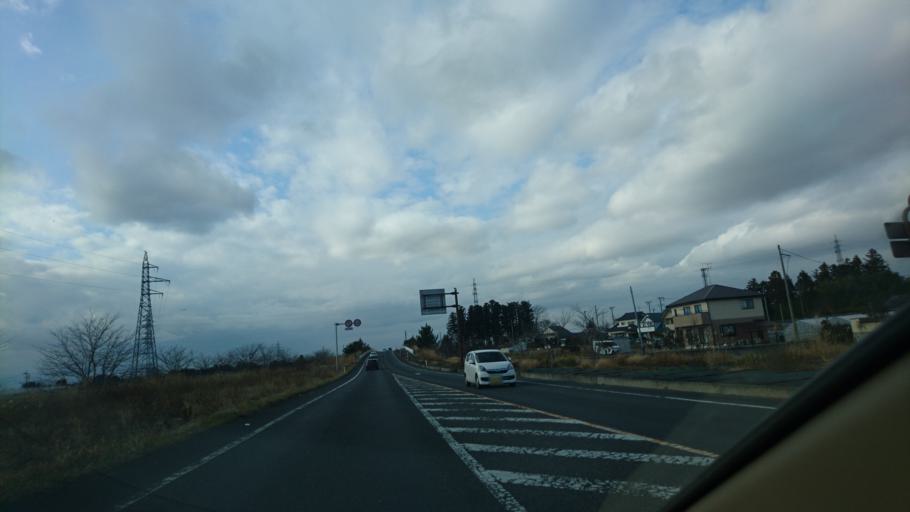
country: JP
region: Miyagi
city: Kogota
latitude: 38.5532
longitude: 141.0486
